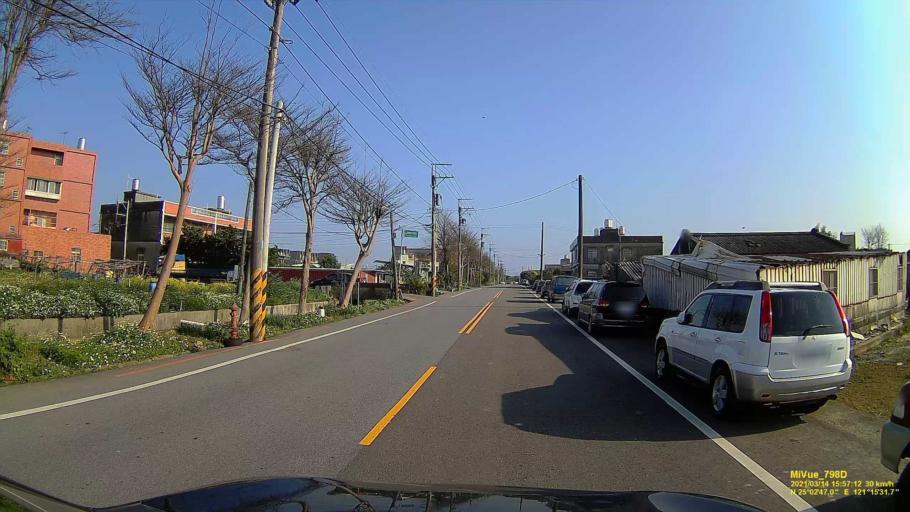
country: TW
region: Taiwan
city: Taoyuan City
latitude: 25.0462
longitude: 121.2589
